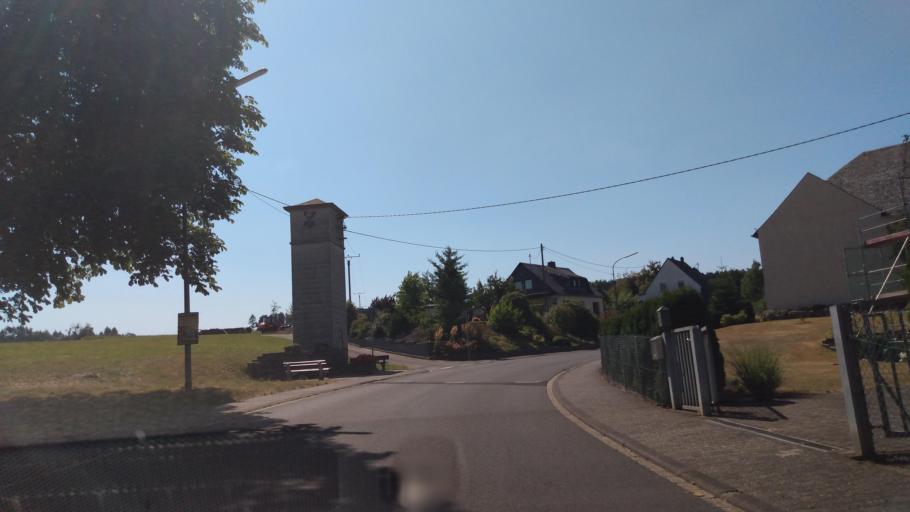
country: DE
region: Rheinland-Pfalz
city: Hochscheid
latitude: 49.8871
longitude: 7.2081
